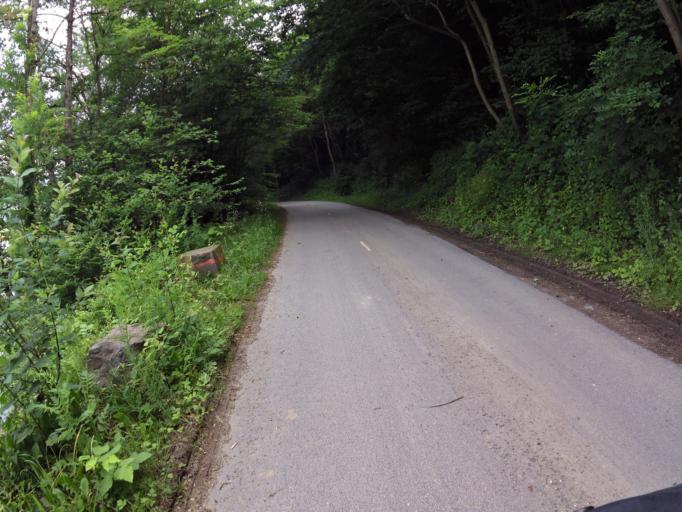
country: BE
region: Wallonia
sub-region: Province de Namur
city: Doische
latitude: 50.1116
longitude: 4.7742
